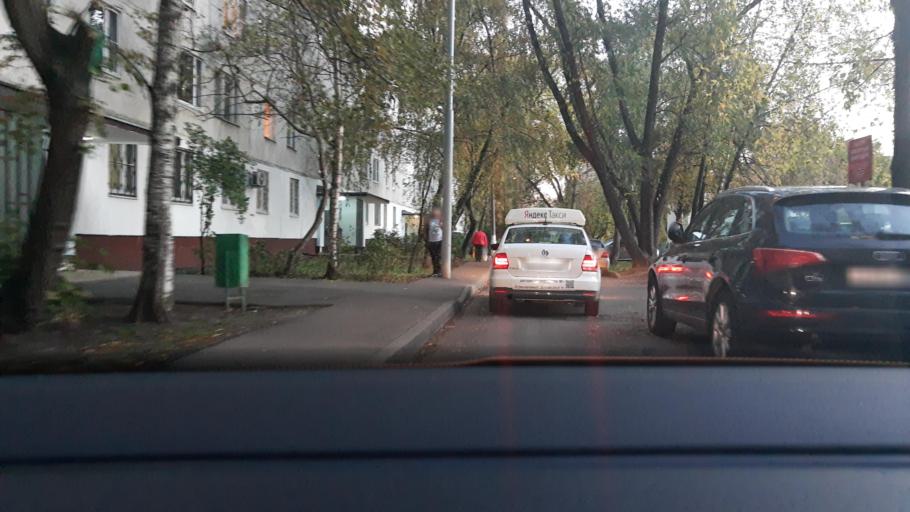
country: RU
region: Moscow
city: Kozeyevo
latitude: 55.8737
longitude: 37.6102
